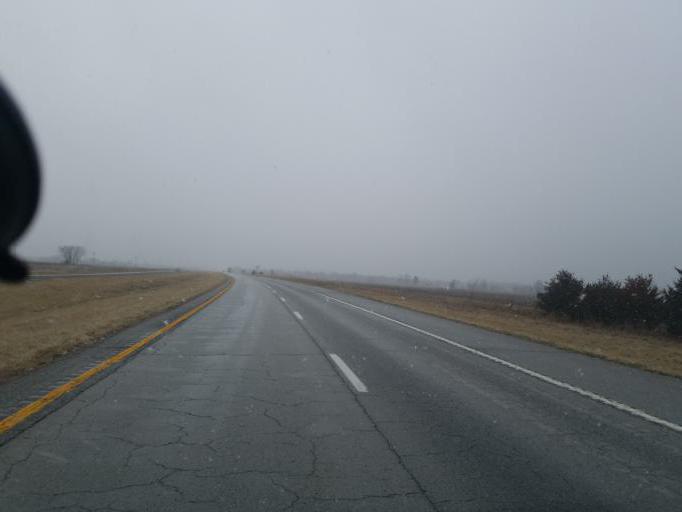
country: US
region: Missouri
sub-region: Macon County
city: La Plata
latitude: 39.9401
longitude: -92.4773
